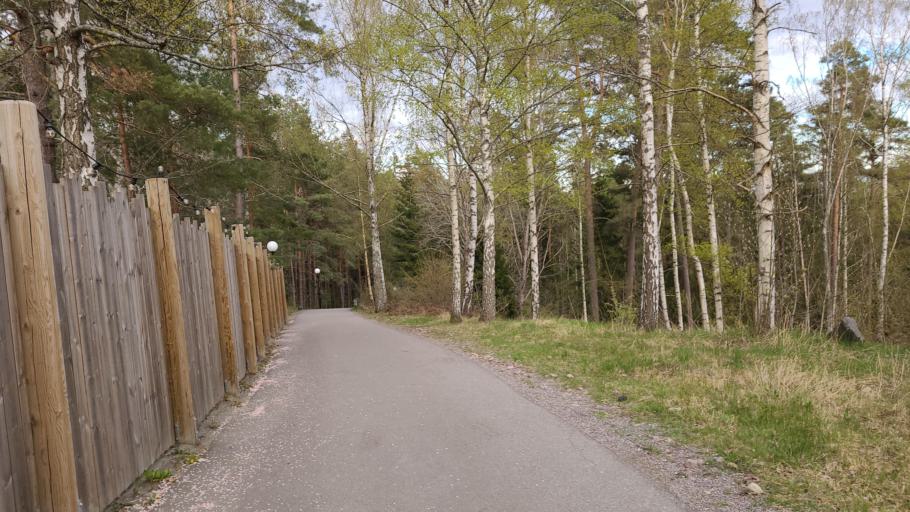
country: SE
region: OEstergoetland
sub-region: Norrkopings Kommun
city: Krokek
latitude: 58.6598
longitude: 16.4504
